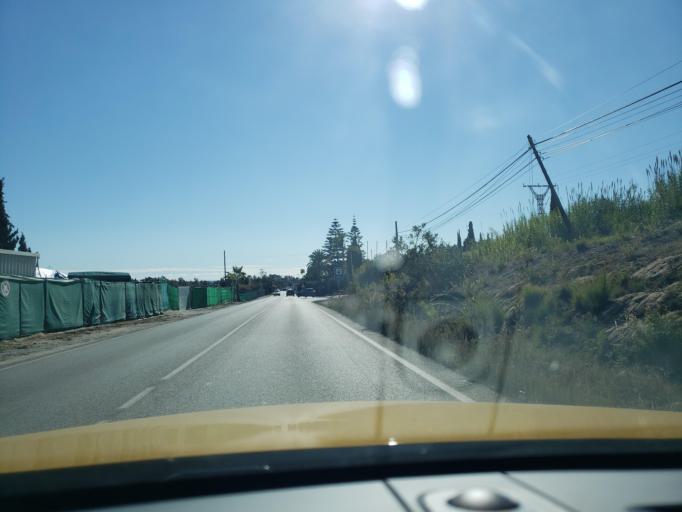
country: ES
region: Andalusia
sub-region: Provincia de Malaga
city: Benahavis
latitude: 36.4761
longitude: -5.0129
